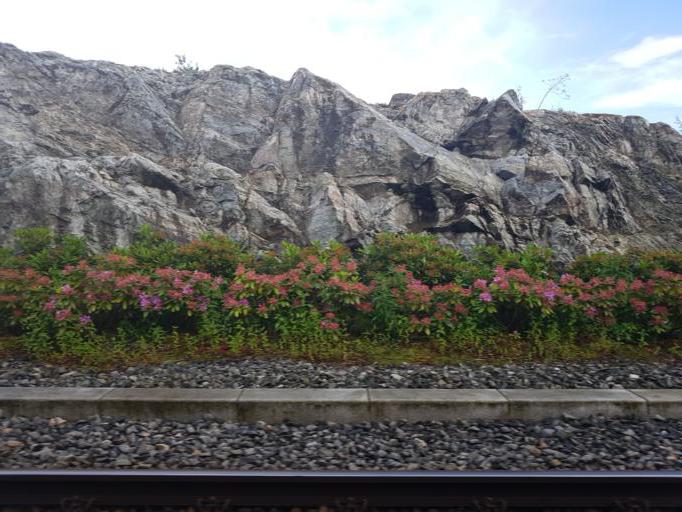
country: NO
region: Hordaland
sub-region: Bergen
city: Ytrebygda
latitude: 60.2938
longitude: 5.2680
